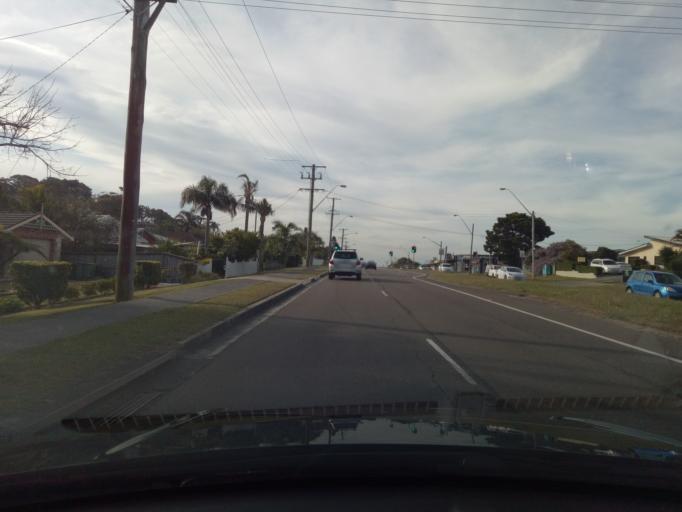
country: AU
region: New South Wales
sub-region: Wyong Shire
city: Bateau Bay
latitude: -33.3903
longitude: 151.4732
